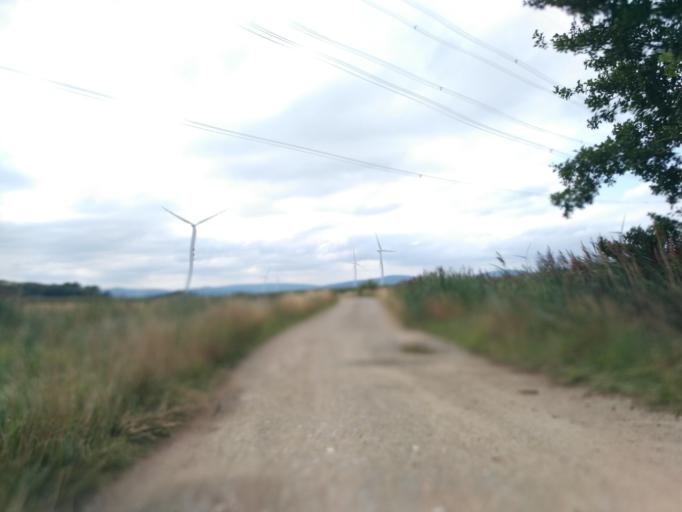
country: PL
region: Subcarpathian Voivodeship
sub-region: Powiat krosnienski
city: Rymanow
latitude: 49.6215
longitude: 21.8463
